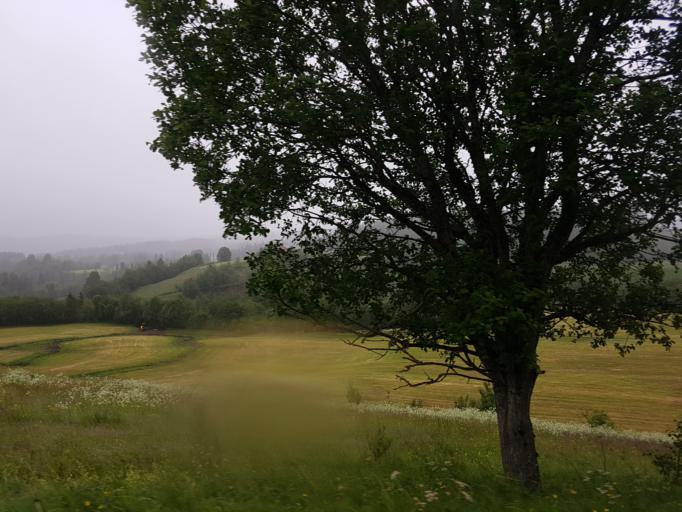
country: NO
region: Sor-Trondelag
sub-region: Selbu
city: Mebonden
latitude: 63.3866
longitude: 11.0757
